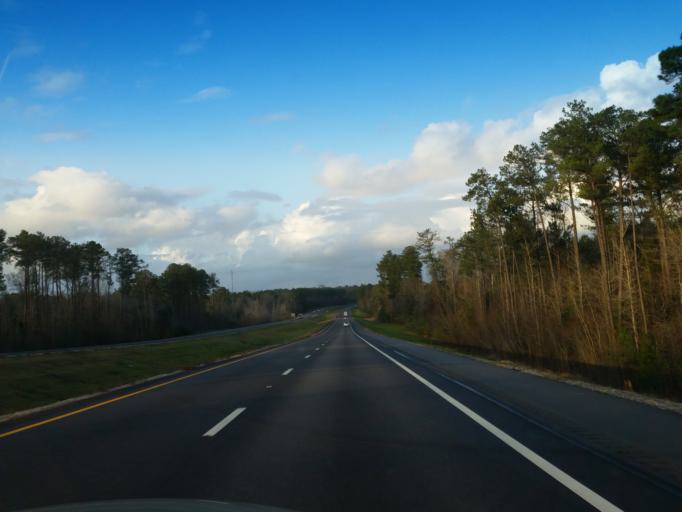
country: US
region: Mississippi
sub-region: Jones County
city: Sharon
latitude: 31.8633
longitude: -89.0465
